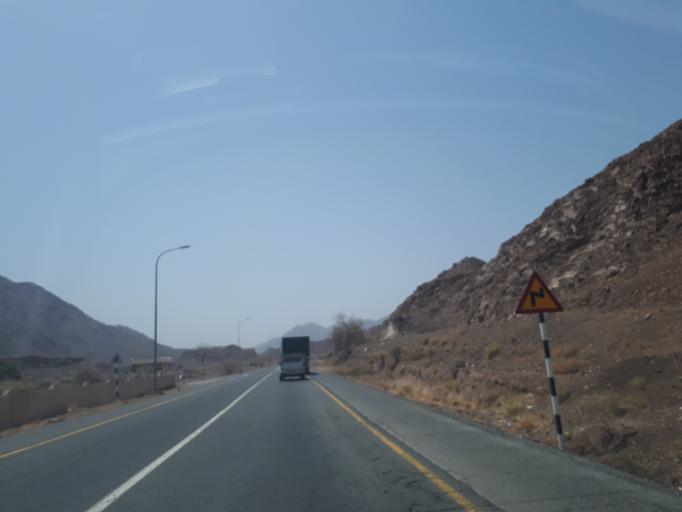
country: OM
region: Muhafazat ad Dakhiliyah
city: Sufalat Sama'il
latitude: 23.2175
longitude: 58.0758
